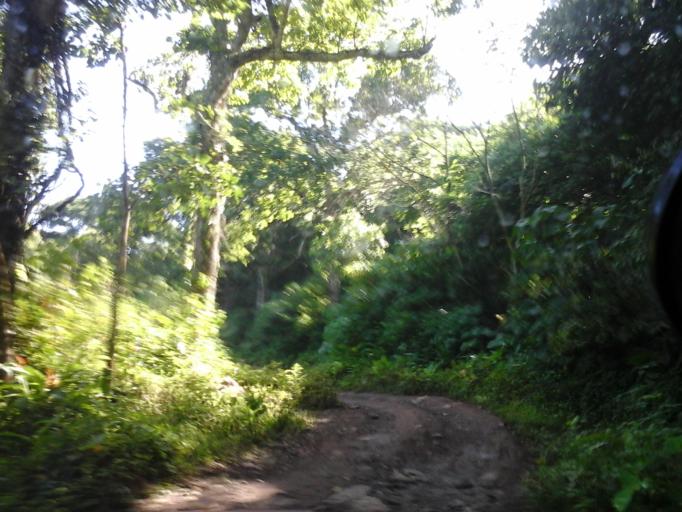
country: CO
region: Cesar
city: San Diego
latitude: 10.2619
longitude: -73.1073
